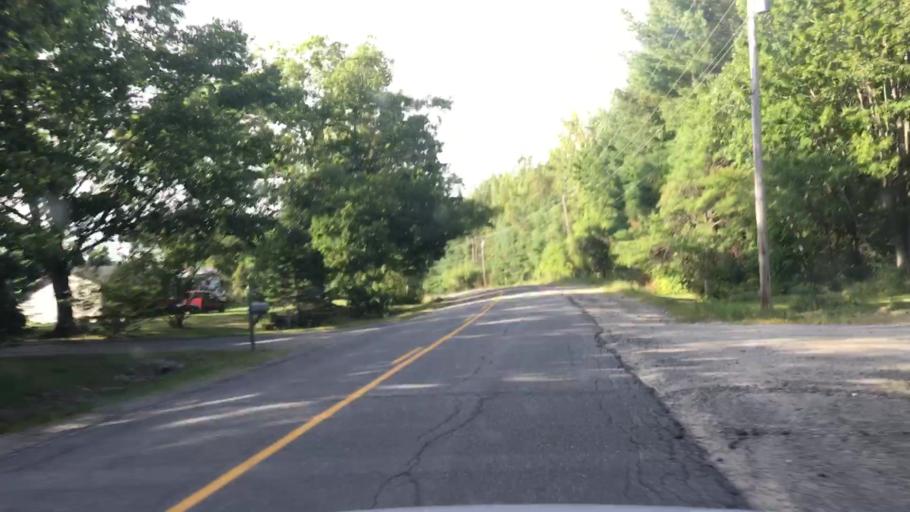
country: US
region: Maine
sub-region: Penobscot County
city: Enfield
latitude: 45.2347
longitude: -68.5440
